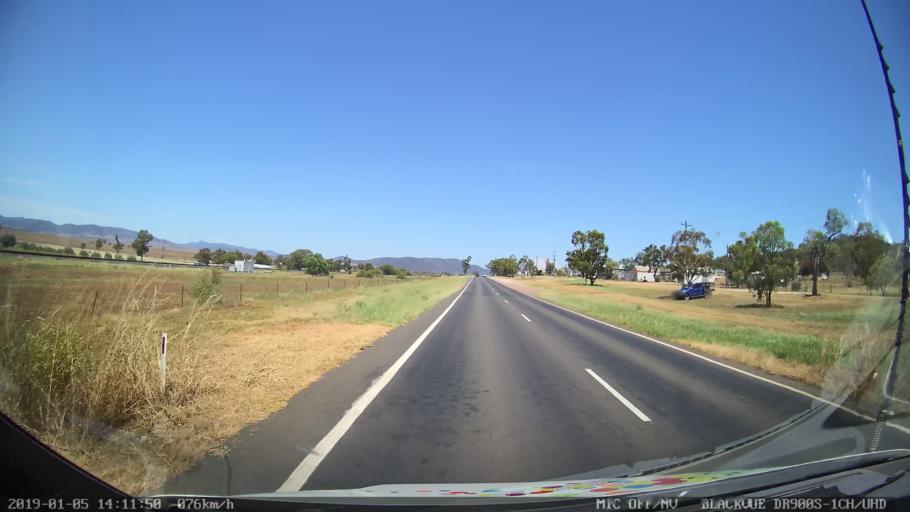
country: AU
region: New South Wales
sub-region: Gunnedah
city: Gunnedah
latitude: -31.2460
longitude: 150.4625
